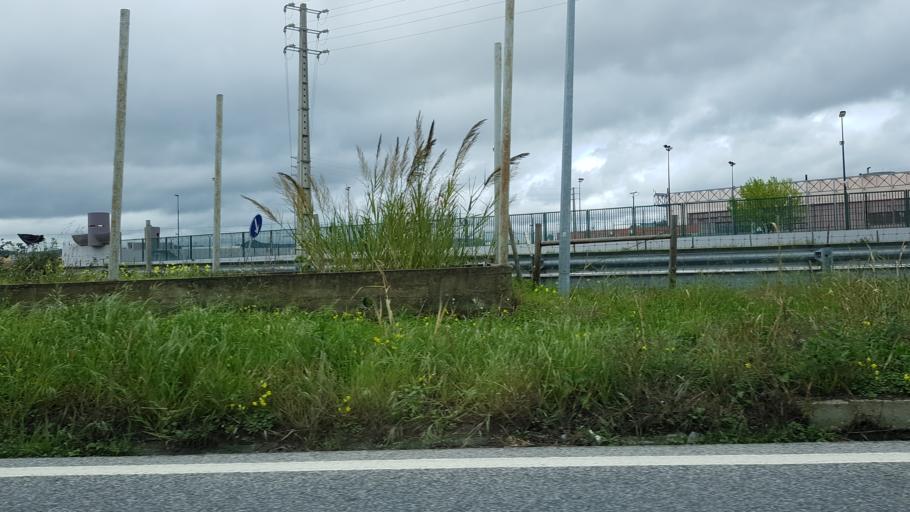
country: PT
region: Lisbon
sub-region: Alenquer
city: Carregado
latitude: 39.0340
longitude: -8.9790
